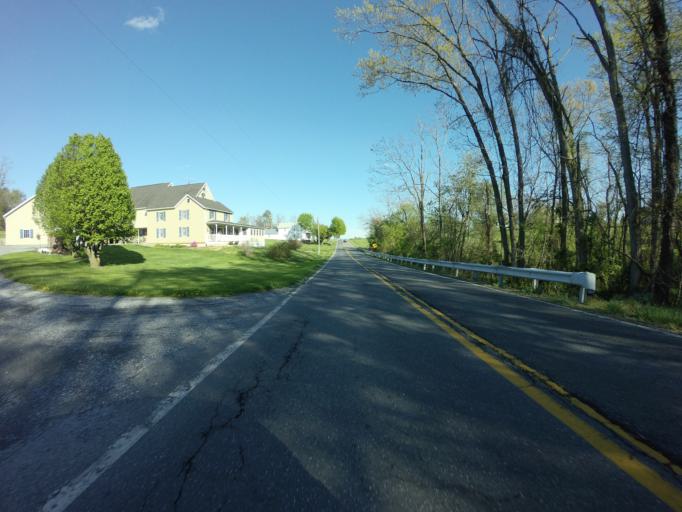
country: US
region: Maryland
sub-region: Frederick County
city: Woodsboro
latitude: 39.5763
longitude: -77.2591
